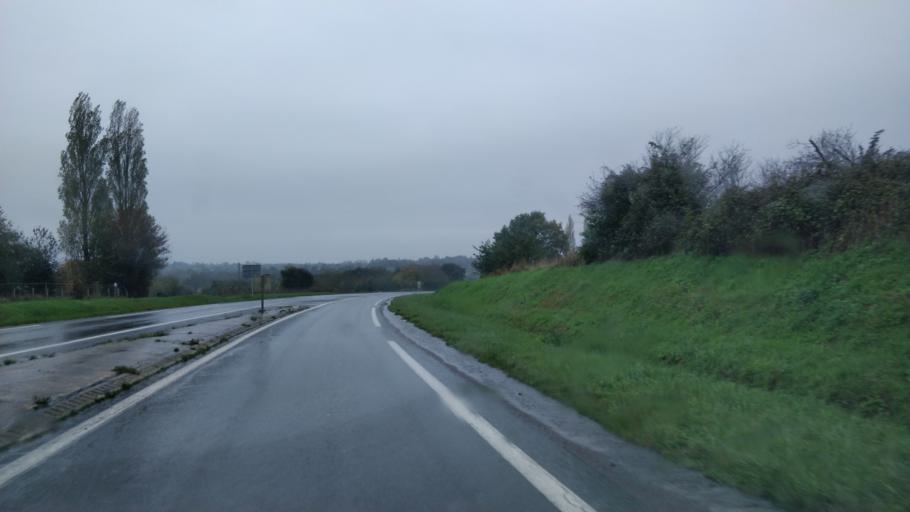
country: FR
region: Lower Normandy
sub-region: Departement de la Manche
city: Saint-Planchers
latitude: 48.8605
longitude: -1.5380
